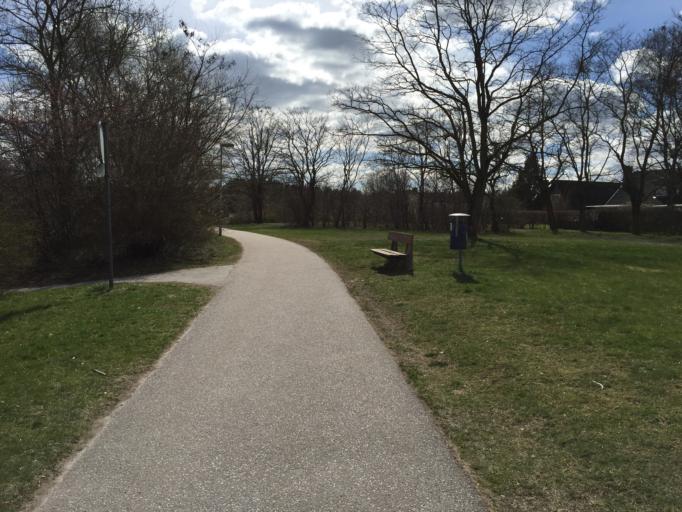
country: SE
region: Skane
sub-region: Lunds Kommun
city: Veberod
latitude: 55.6279
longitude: 13.4958
